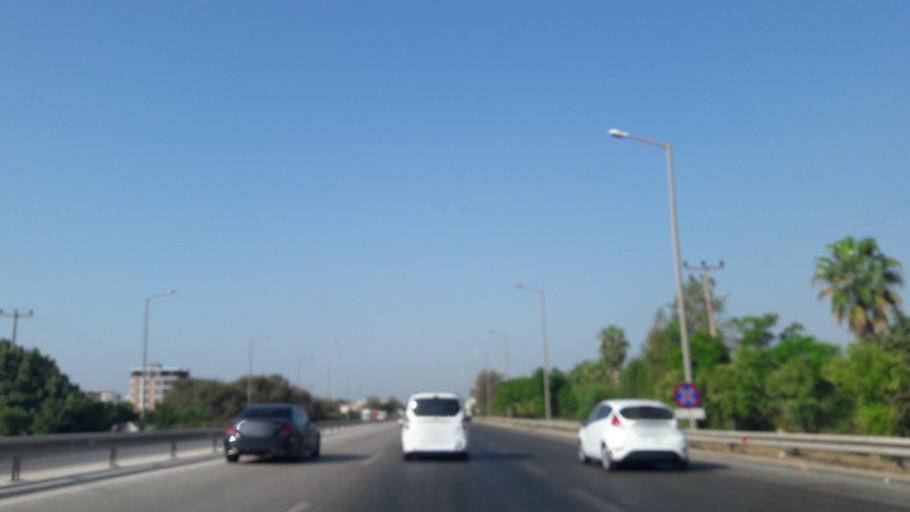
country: TR
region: Adana
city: Yuregir
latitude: 37.0252
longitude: 35.4137
